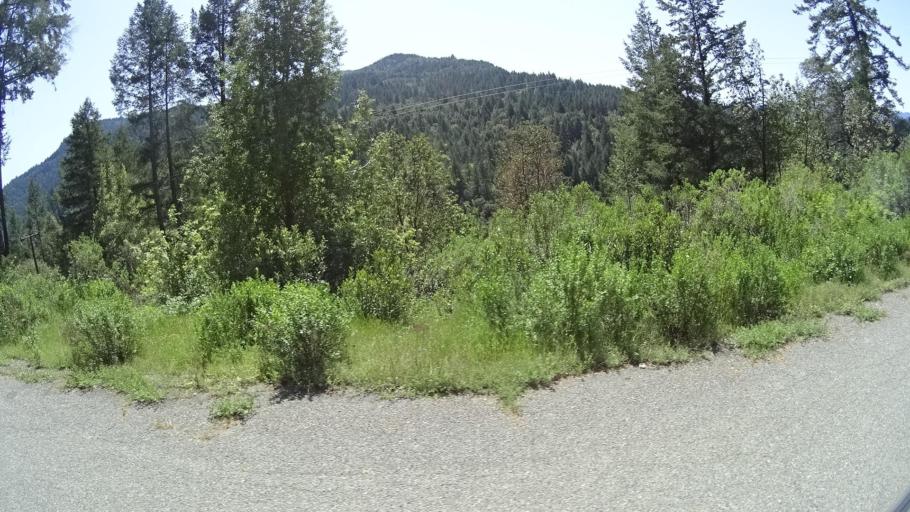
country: US
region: California
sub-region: Humboldt County
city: Redway
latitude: 40.1942
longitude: -123.5511
